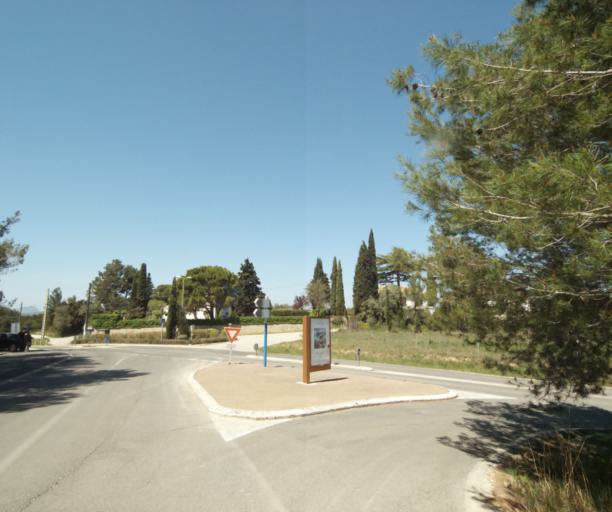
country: FR
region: Languedoc-Roussillon
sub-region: Departement de l'Herault
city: Saint-Genies-des-Mourgues
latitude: 43.6986
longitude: 4.0239
